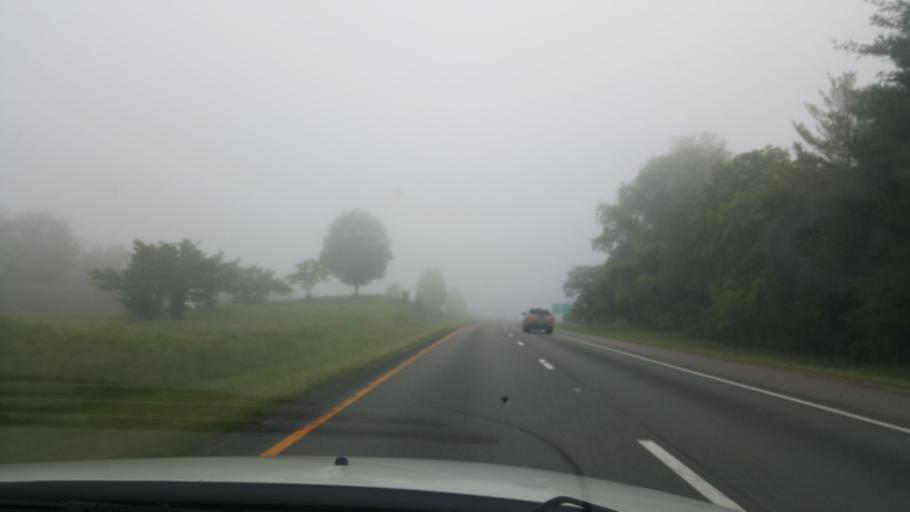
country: US
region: Virginia
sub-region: Montgomery County
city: Christiansburg
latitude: 37.1177
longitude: -80.4140
